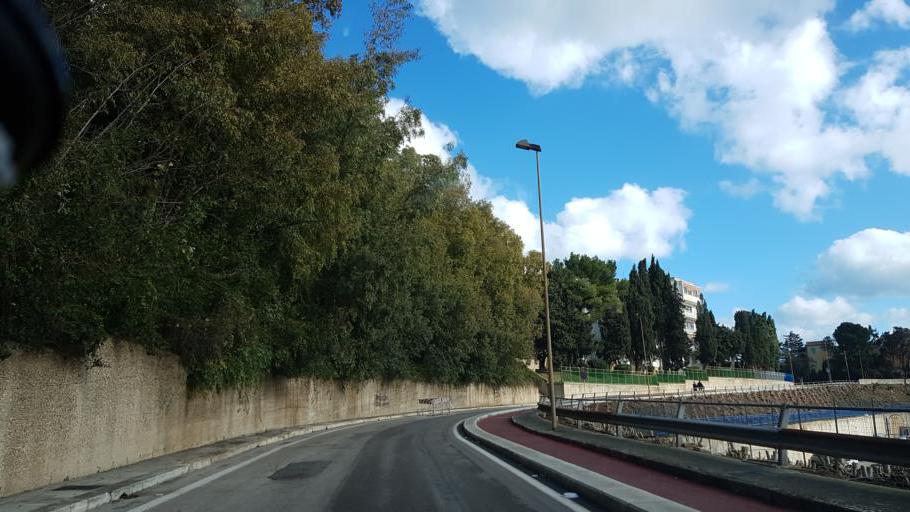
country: IT
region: Apulia
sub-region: Provincia di Brindisi
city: Brindisi
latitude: 40.6437
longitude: 17.9356
